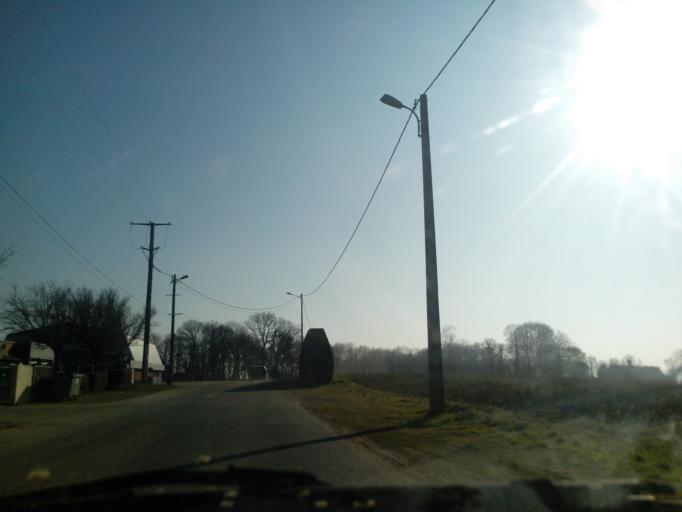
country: FR
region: Brittany
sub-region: Departement du Morbihan
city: Meneac
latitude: 48.1369
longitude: -2.4529
